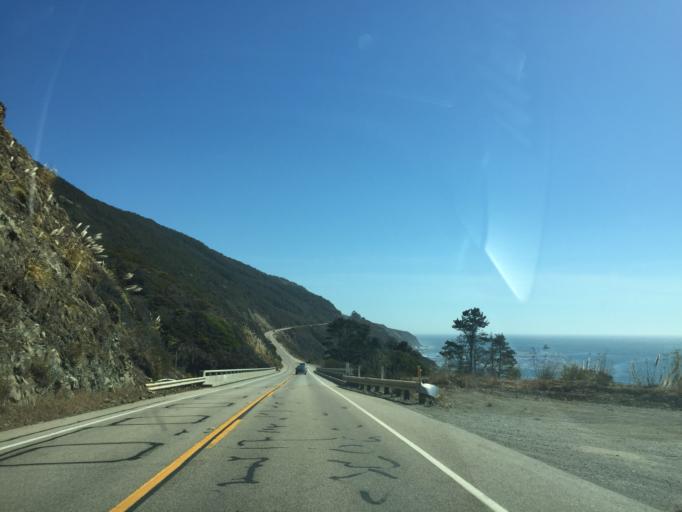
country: US
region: California
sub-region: Monterey County
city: Greenfield
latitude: 36.0451
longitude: -121.5852
